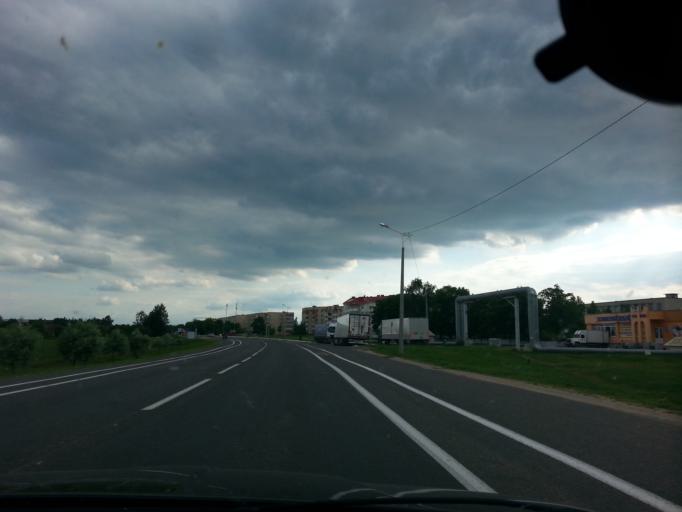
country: BY
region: Minsk
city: Myadzyel
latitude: 54.8736
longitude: 26.9394
